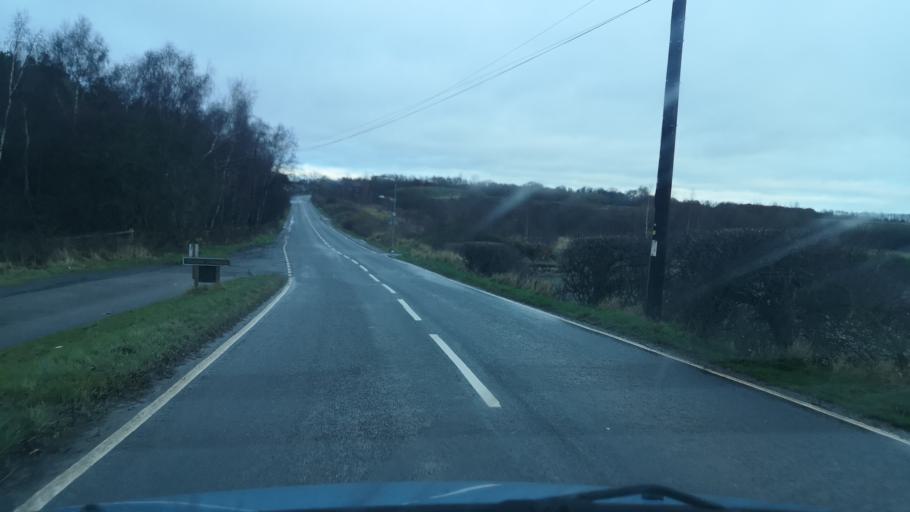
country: GB
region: England
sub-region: City and Borough of Wakefield
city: Fitzwilliam
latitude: 53.6433
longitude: -1.3955
